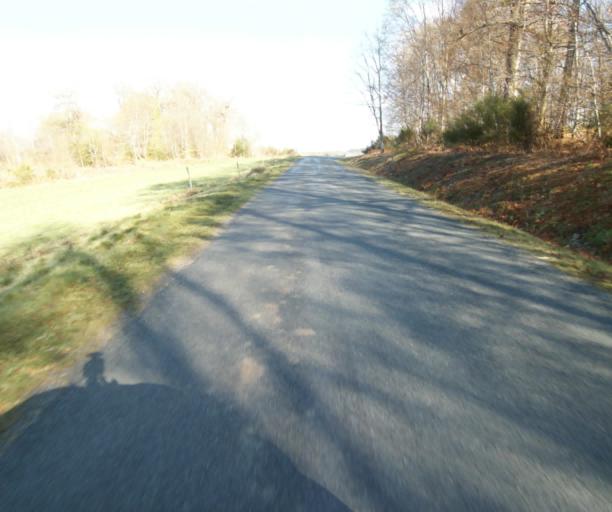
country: FR
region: Limousin
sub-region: Departement de la Correze
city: Correze
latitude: 45.2974
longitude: 1.8698
